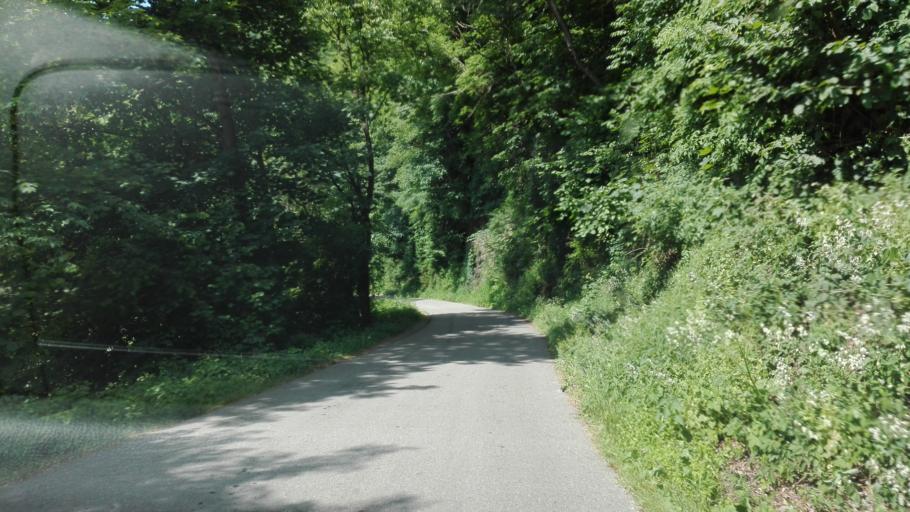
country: AT
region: Upper Austria
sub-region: Politischer Bezirk Rohrbach
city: Atzesberg
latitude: 48.4312
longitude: 13.8760
